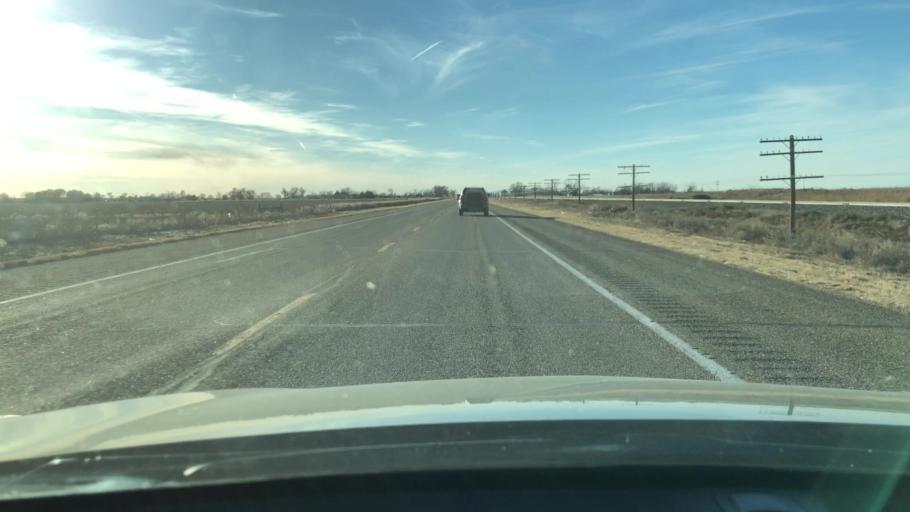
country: US
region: Colorado
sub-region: Prowers County
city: Lamar
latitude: 38.0831
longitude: -102.4014
